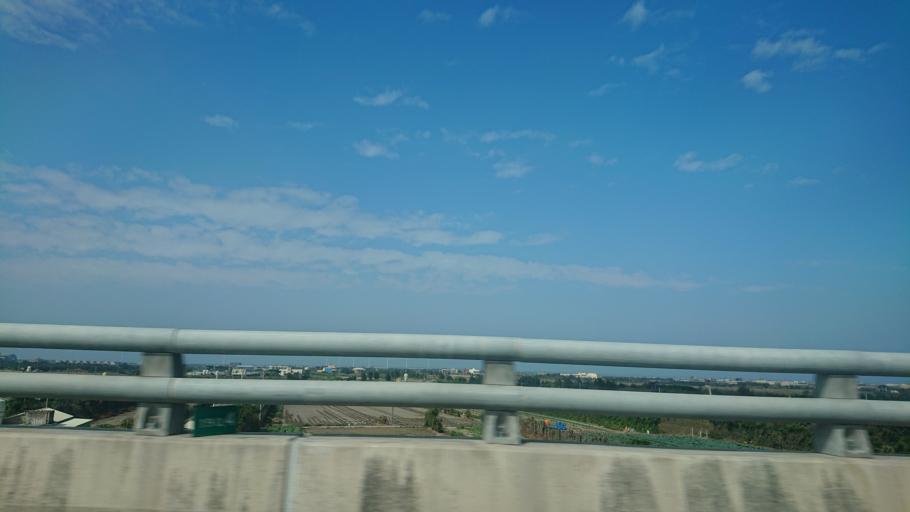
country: TW
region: Taiwan
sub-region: Changhua
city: Chang-hua
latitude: 23.9795
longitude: 120.3638
